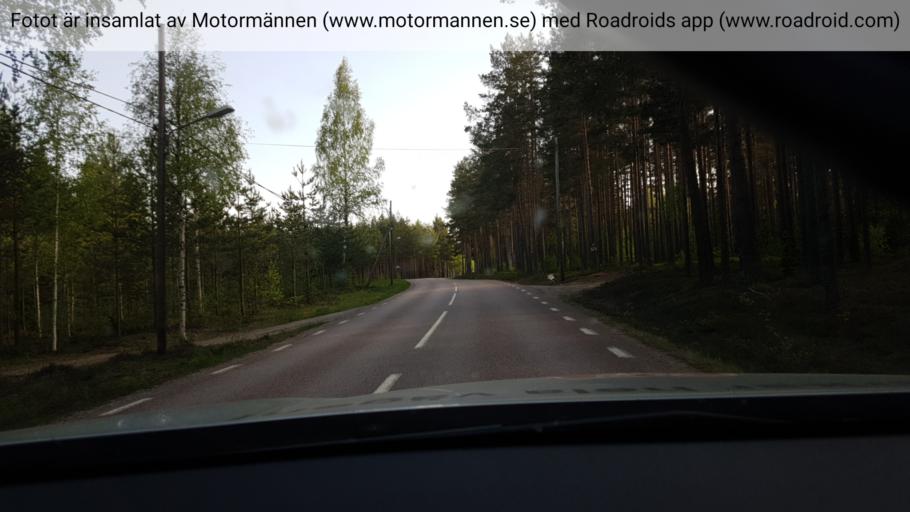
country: SE
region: Gaevleborg
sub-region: Sandvikens Kommun
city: Arsunda
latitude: 60.4592
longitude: 16.7052
